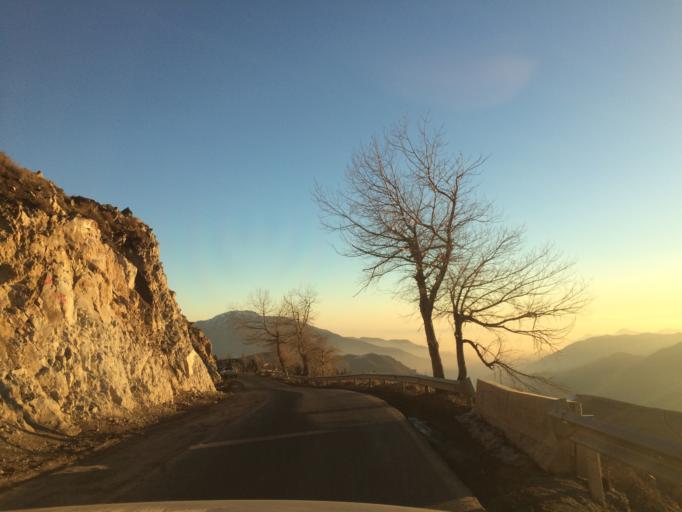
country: CL
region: Santiago Metropolitan
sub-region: Provincia de Santiago
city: Villa Presidente Frei, Nunoa, Santiago, Chile
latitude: -33.3480
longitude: -70.3066
